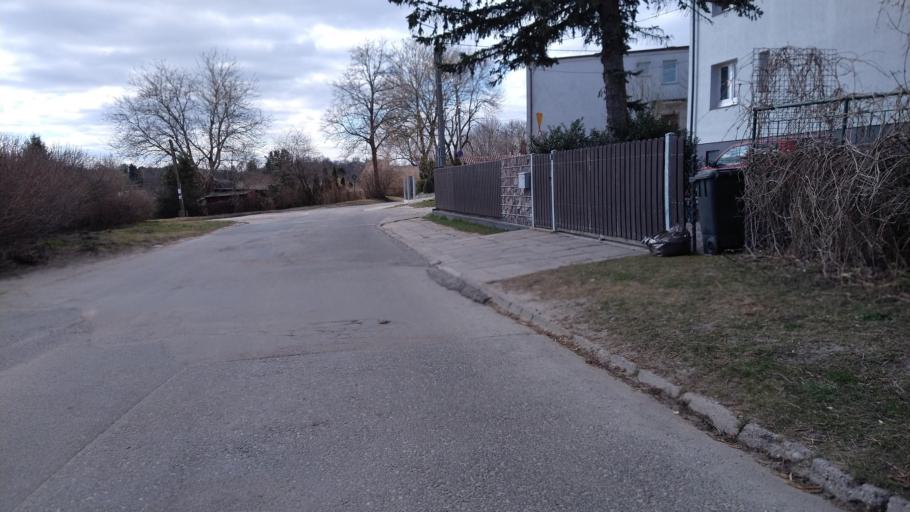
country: PL
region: Warmian-Masurian Voivodeship
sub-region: Powiat olsztynski
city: Olsztyn
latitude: 53.8001
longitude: 20.4900
